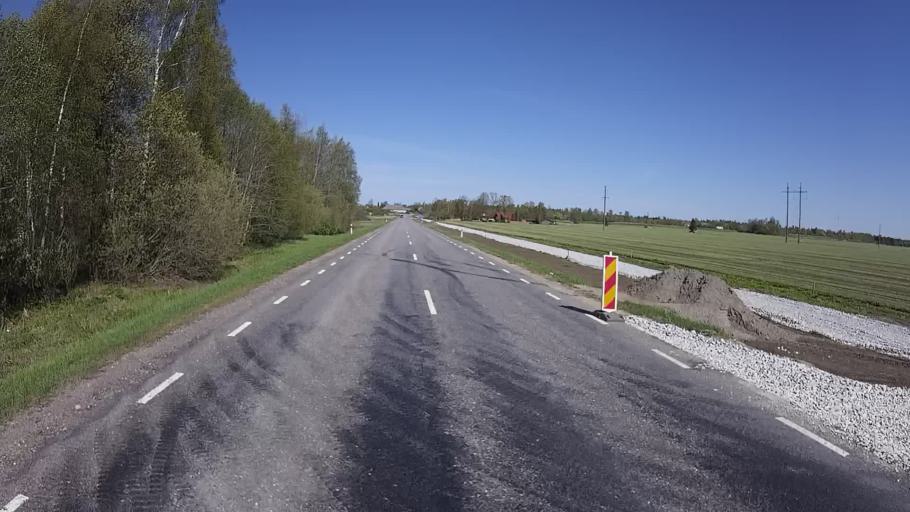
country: EE
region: Paernumaa
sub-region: Tootsi vald
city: Tootsi
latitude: 58.4993
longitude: 24.8011
